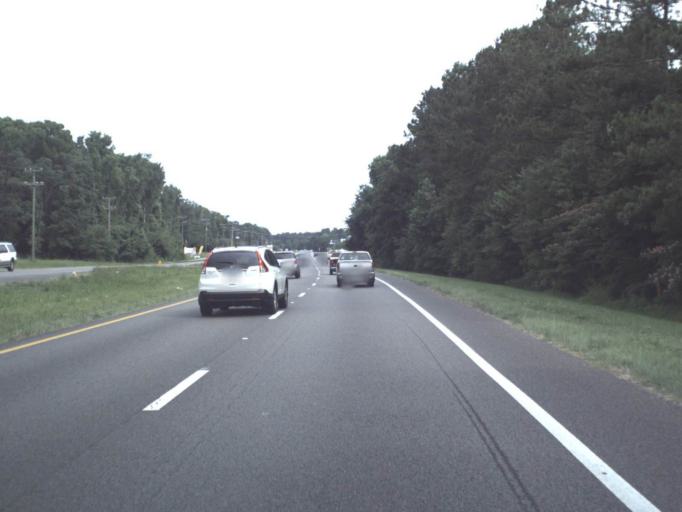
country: US
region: Florida
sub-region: Clay County
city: Green Cove Springs
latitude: 30.0212
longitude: -81.7052
